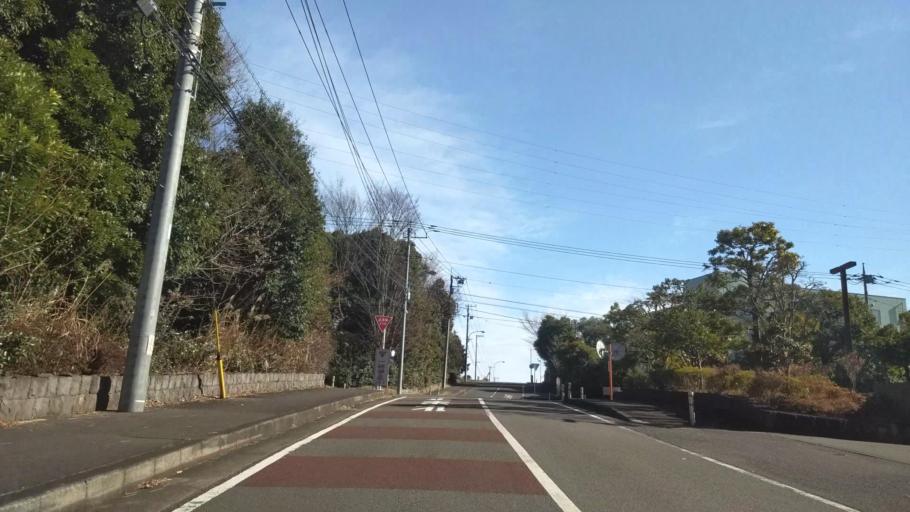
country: JP
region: Kanagawa
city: Hadano
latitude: 35.3444
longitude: 139.2249
